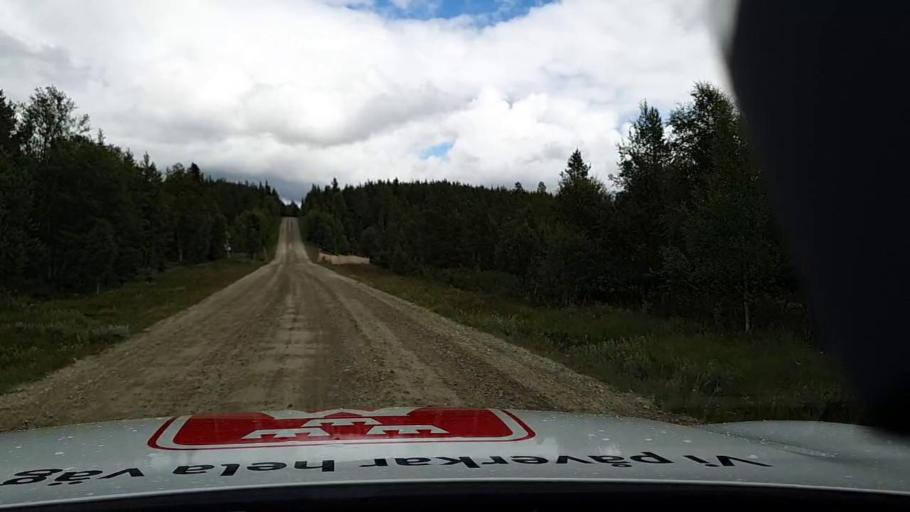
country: SE
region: Jaemtland
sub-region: Are Kommun
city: Jarpen
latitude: 62.6004
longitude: 13.2644
